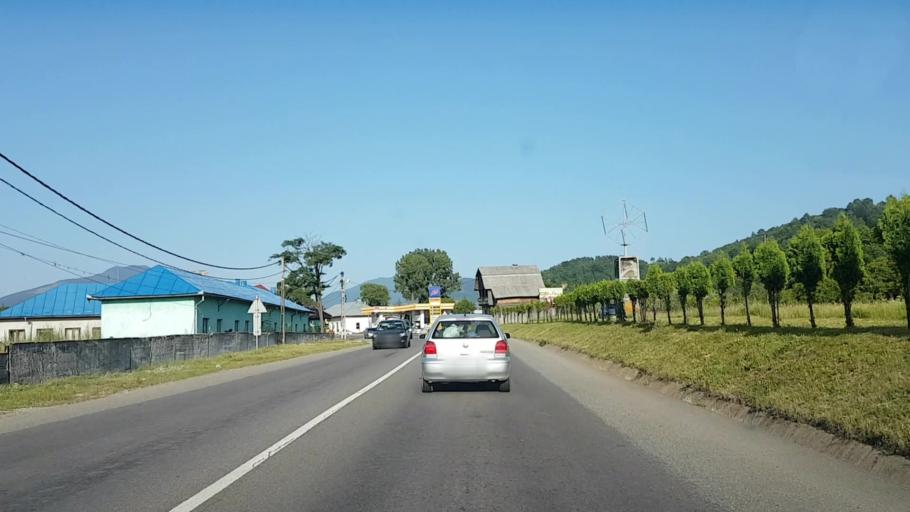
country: RO
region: Bistrita-Nasaud
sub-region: Comuna Prundu Bargaului
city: Susenii Bargaului
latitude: 47.2183
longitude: 24.7117
